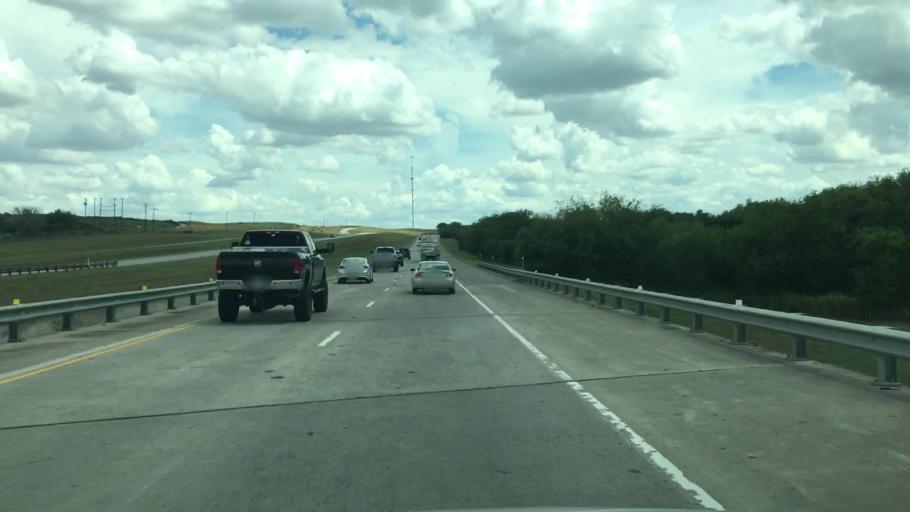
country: US
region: Texas
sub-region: San Patricio County
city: Mathis
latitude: 28.2617
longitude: -97.9307
